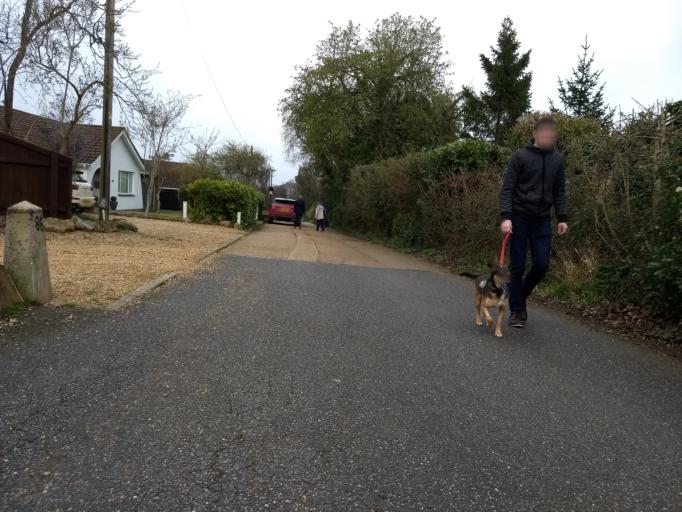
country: GB
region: England
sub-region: Isle of Wight
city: Ryde
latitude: 50.7295
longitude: -1.1740
